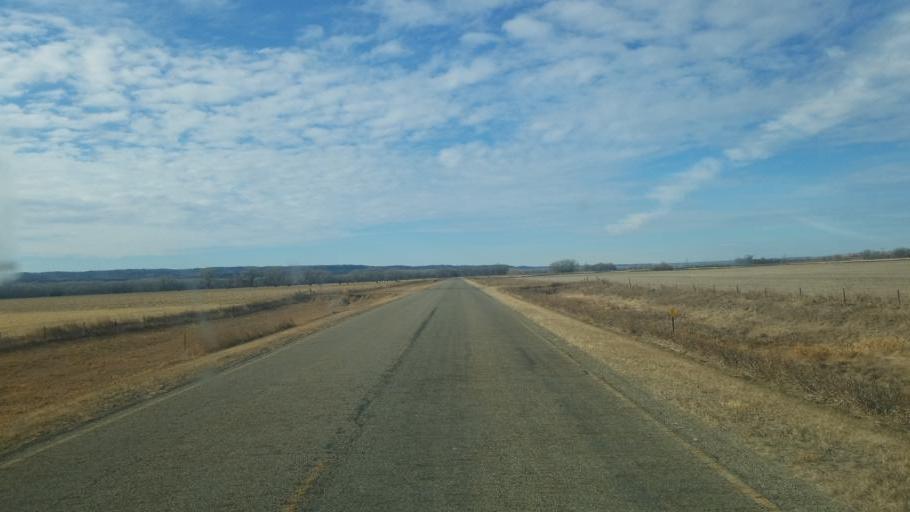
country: US
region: South Dakota
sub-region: Charles Mix County
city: Wagner
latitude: 42.8928
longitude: -98.2931
